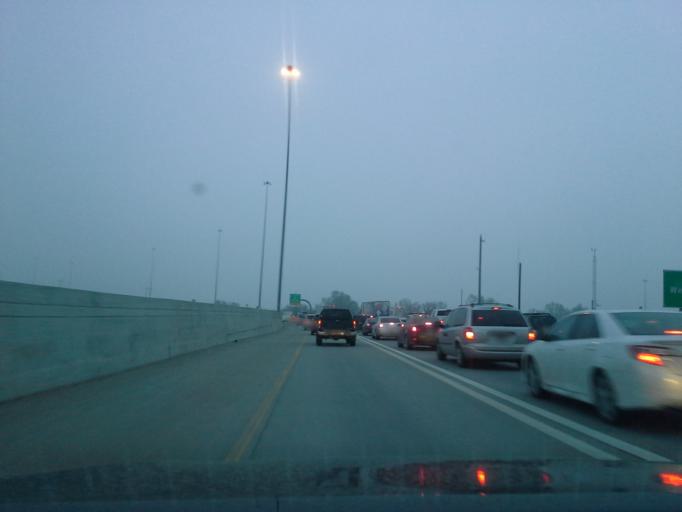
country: US
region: Utah
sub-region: Salt Lake County
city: Midvale
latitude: 40.6377
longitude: -111.9043
